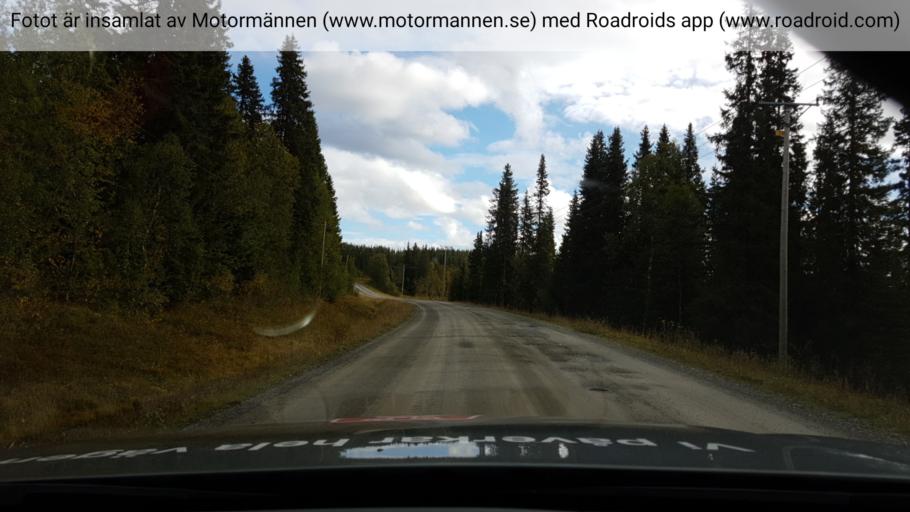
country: SE
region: Jaemtland
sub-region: Are Kommun
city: Are
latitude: 63.7045
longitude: 12.7520
